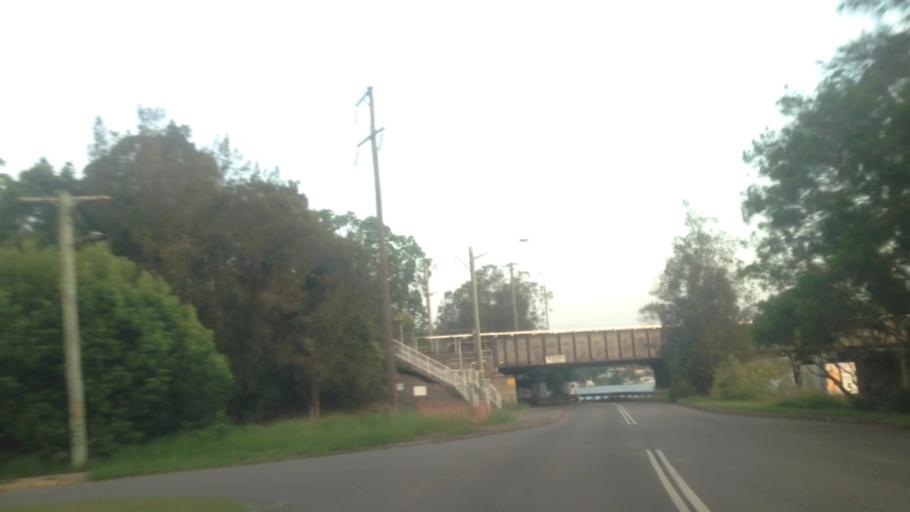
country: AU
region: New South Wales
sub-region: Lake Macquarie Shire
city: Dora Creek
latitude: -33.0836
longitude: 151.5002
